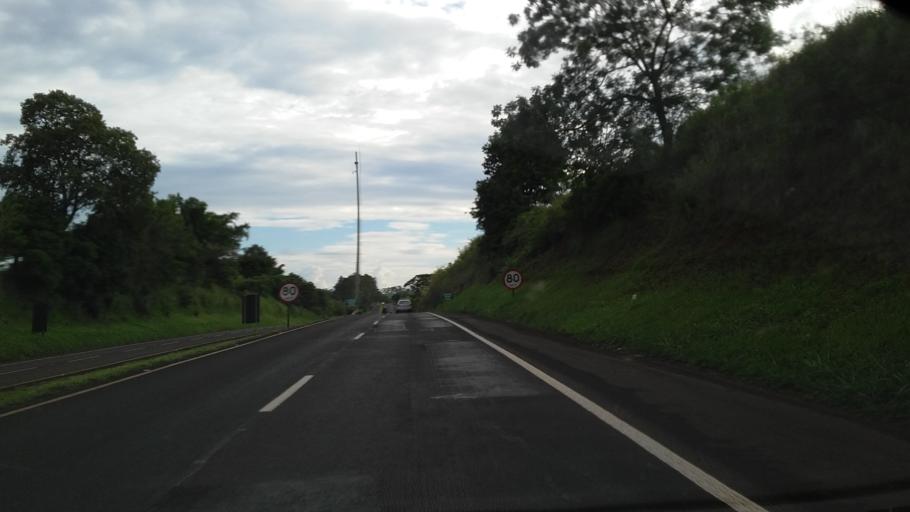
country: BR
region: Parana
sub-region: Paicandu
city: Paicandu
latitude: -23.5160
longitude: -52.0273
